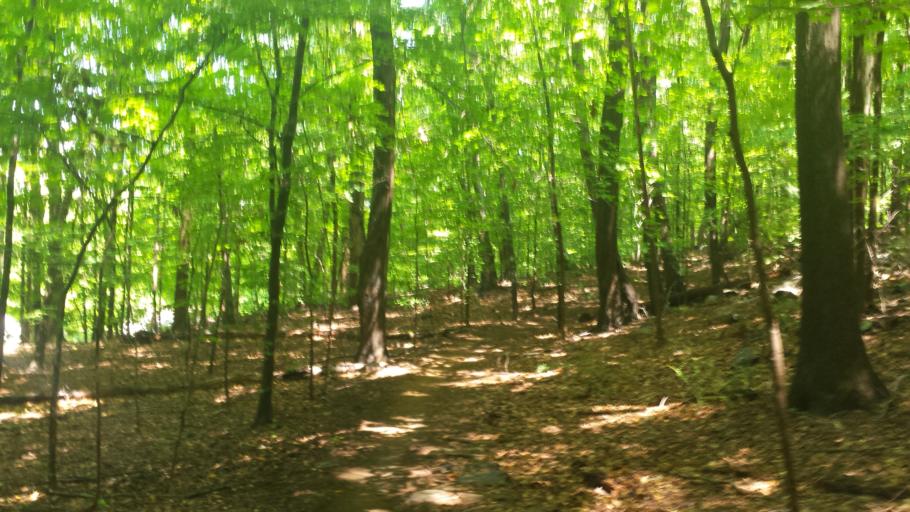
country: US
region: New York
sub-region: Westchester County
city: Hawthorne
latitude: 41.1207
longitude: -73.8006
